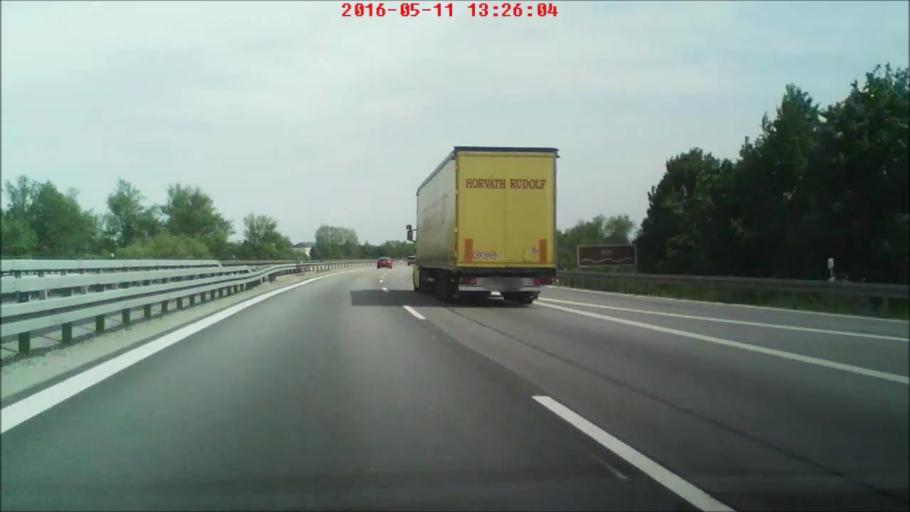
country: AT
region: Upper Austria
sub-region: Politischer Bezirk Scharding
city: Sankt Florian am Inn
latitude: 48.4144
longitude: 13.4199
